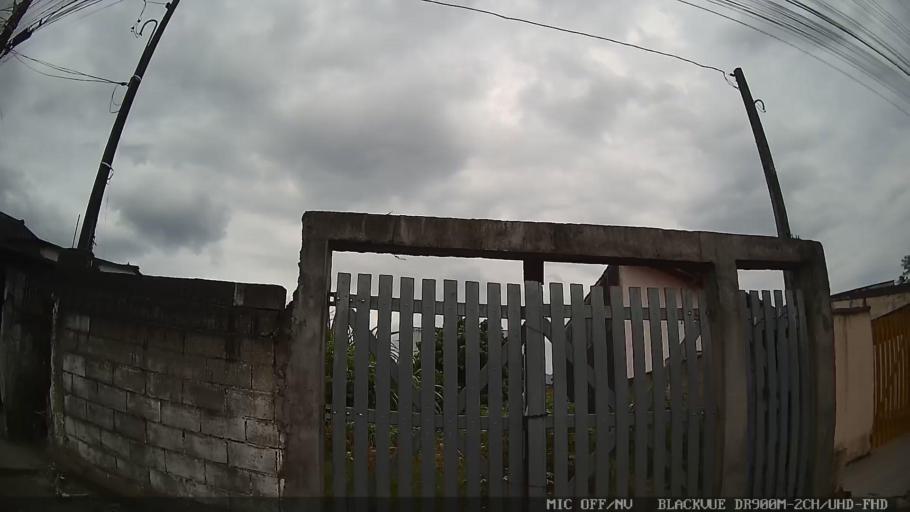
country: BR
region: Sao Paulo
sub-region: Caraguatatuba
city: Caraguatatuba
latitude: -23.6727
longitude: -45.4484
